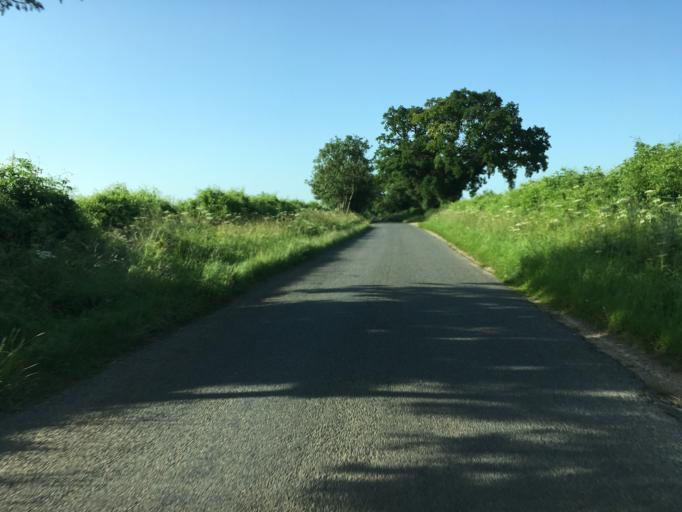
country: GB
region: England
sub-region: Oxfordshire
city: Burford
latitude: 51.8024
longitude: -1.7019
